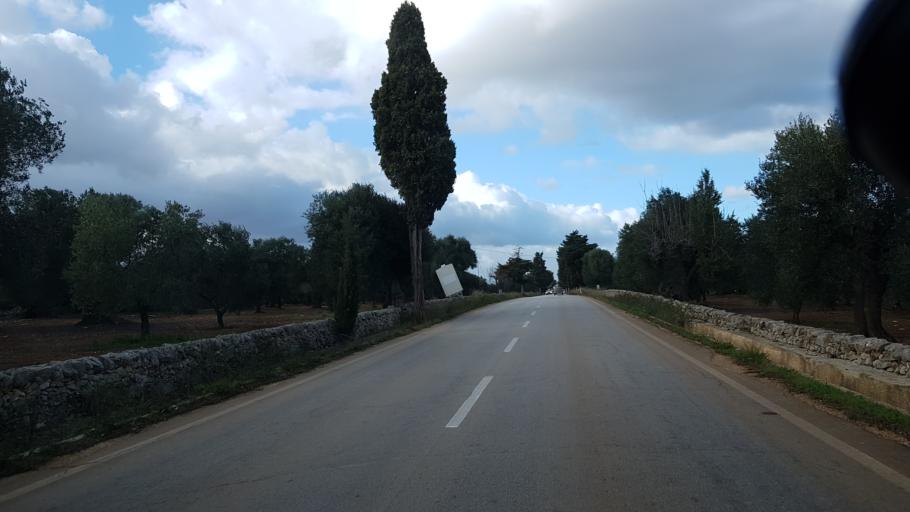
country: IT
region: Apulia
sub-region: Provincia di Brindisi
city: Montalbano
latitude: 40.7751
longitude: 17.4965
